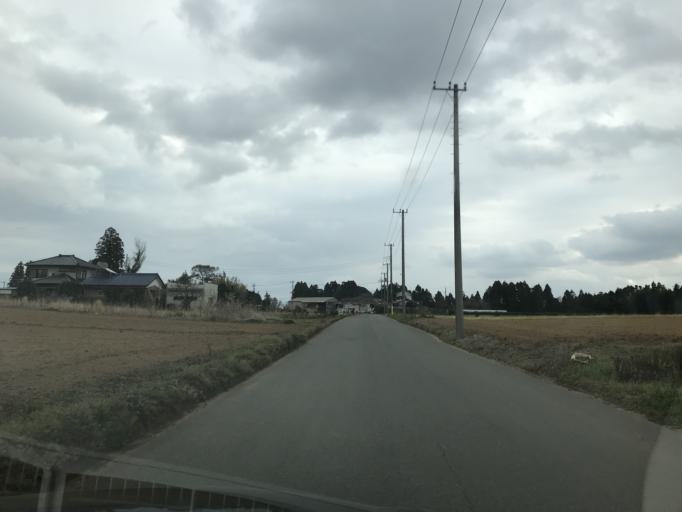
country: JP
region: Chiba
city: Sawara
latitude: 35.8509
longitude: 140.4766
